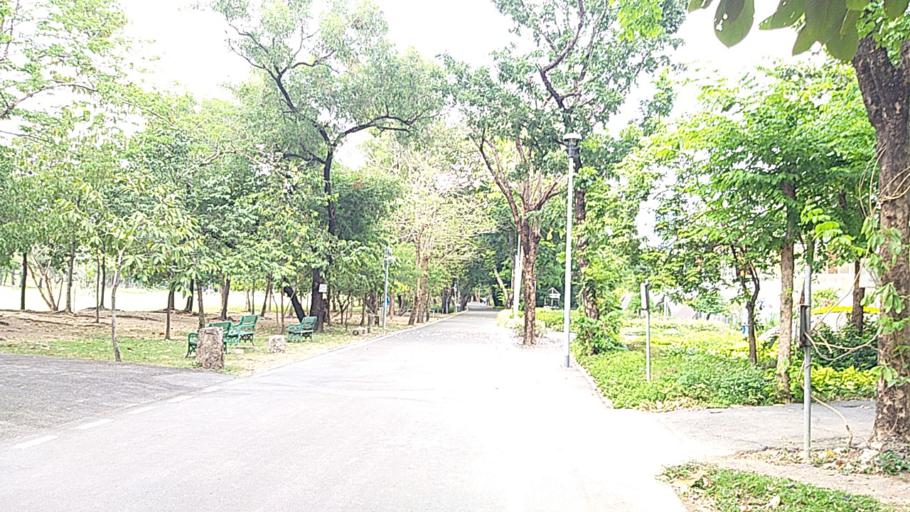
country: TH
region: Bangkok
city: Bang Sue
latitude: 13.8093
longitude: 100.5544
